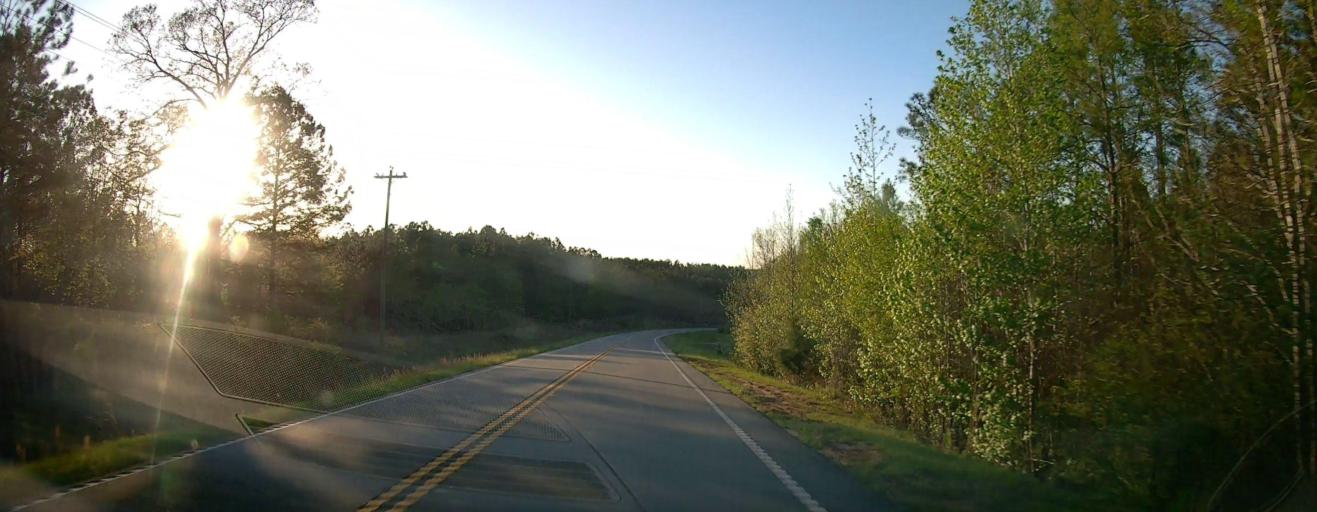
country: US
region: Georgia
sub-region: Talbot County
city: Talbotton
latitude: 32.5442
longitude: -84.5296
